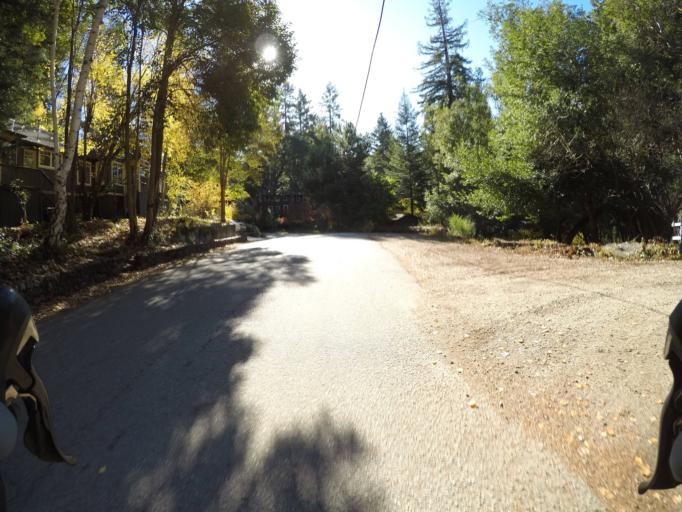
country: US
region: California
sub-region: Santa Cruz County
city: Mount Hermon
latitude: 37.0523
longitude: -122.0545
